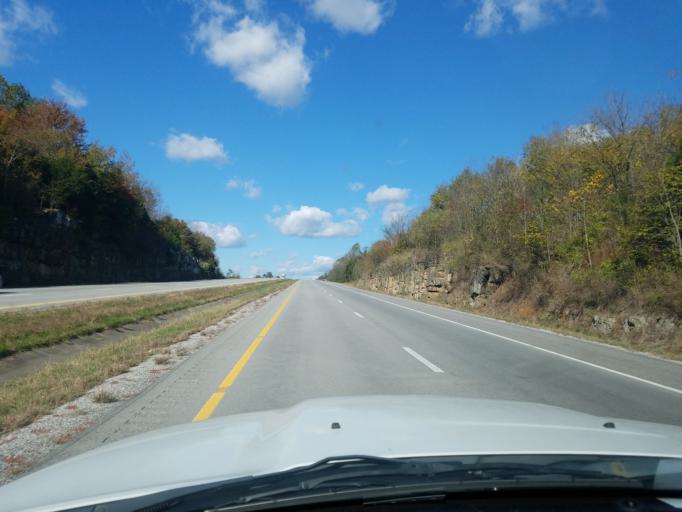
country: US
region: Kentucky
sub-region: Barren County
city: Glasgow
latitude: 36.9992
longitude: -85.9953
